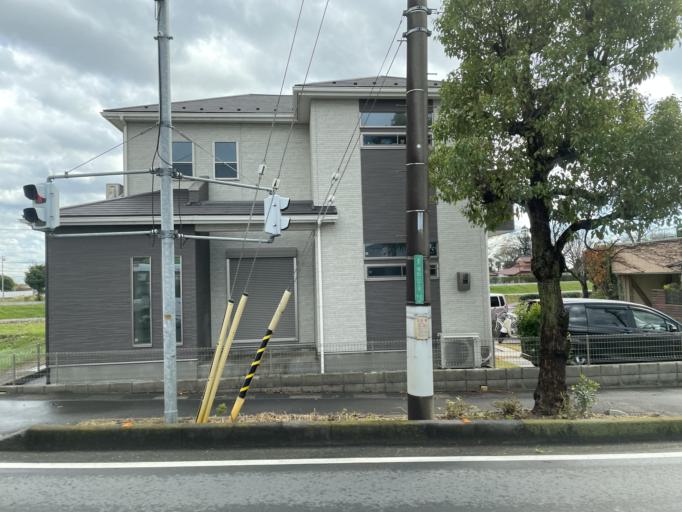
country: JP
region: Saitama
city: Koshigaya
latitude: 35.9123
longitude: 139.8009
